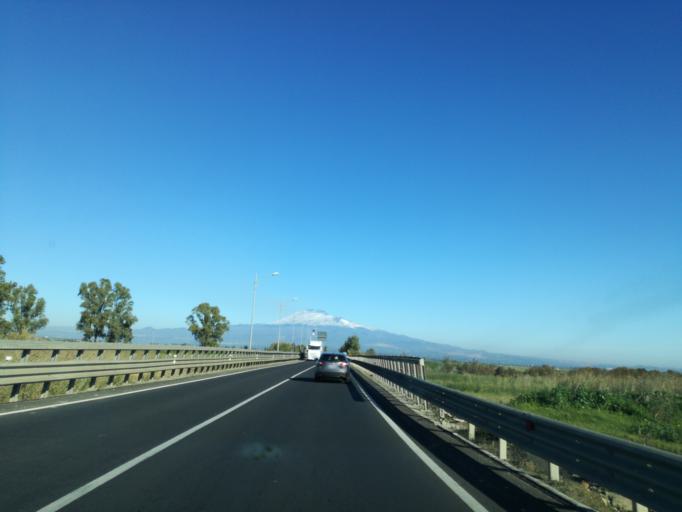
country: IT
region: Sicily
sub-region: Catania
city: Scordia
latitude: 37.3939
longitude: 14.8820
